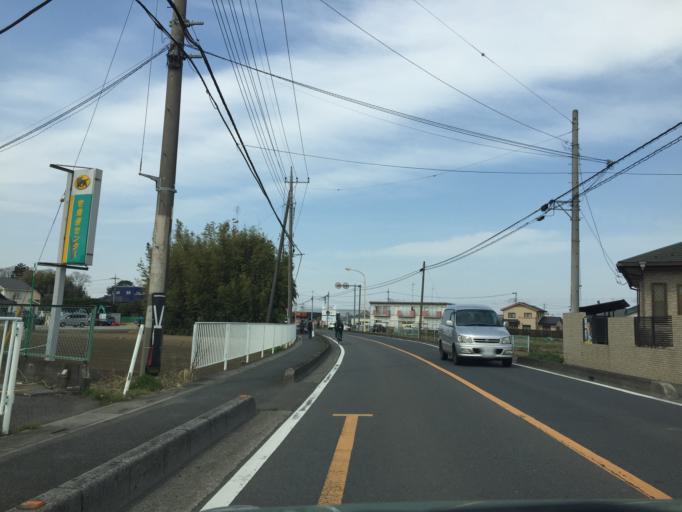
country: JP
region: Saitama
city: Yono
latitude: 35.8735
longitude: 139.5990
